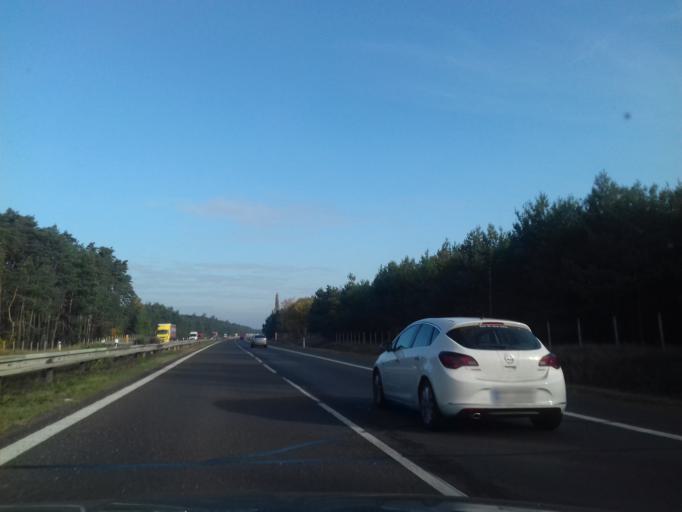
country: SK
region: Bratislavsky
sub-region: Okres Malacky
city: Malacky
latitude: 48.3708
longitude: 17.0200
